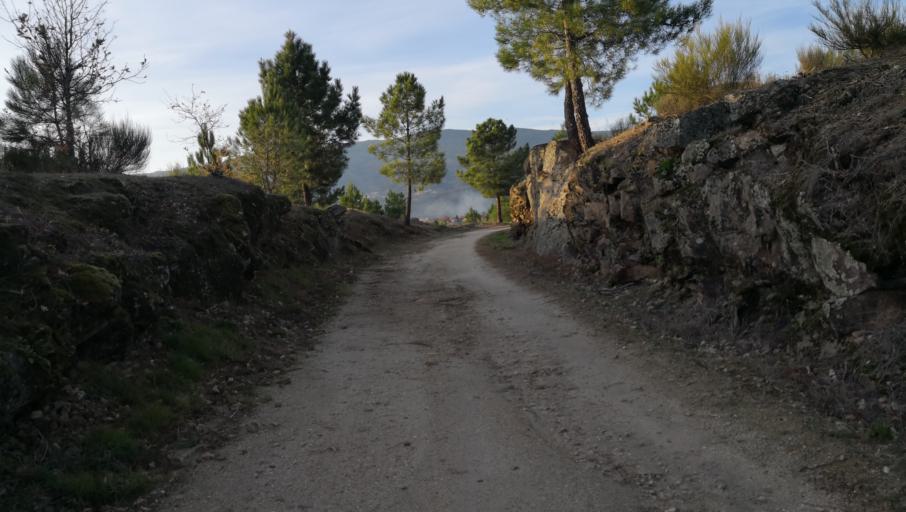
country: PT
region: Vila Real
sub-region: Vila Real
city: Vila Real
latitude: 41.3345
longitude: -7.7086
